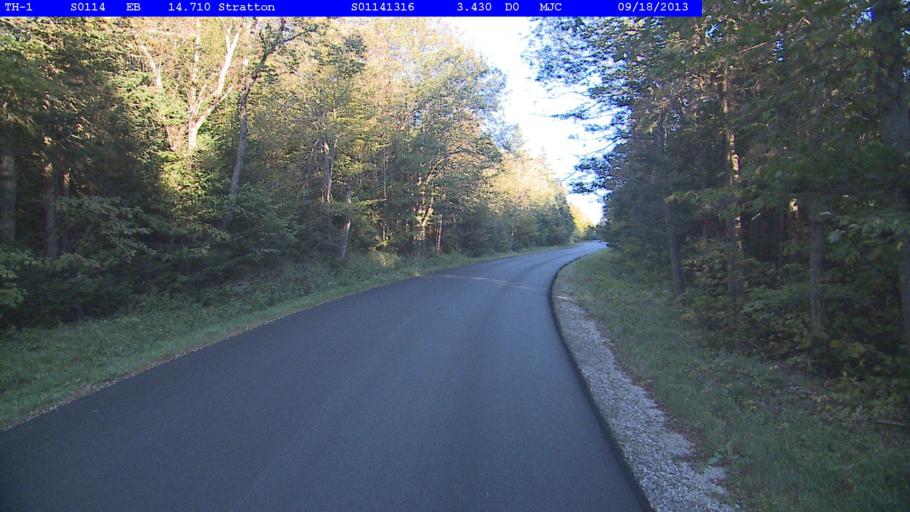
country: US
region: Vermont
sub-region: Bennington County
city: Manchester Center
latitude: 43.0574
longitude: -72.9391
